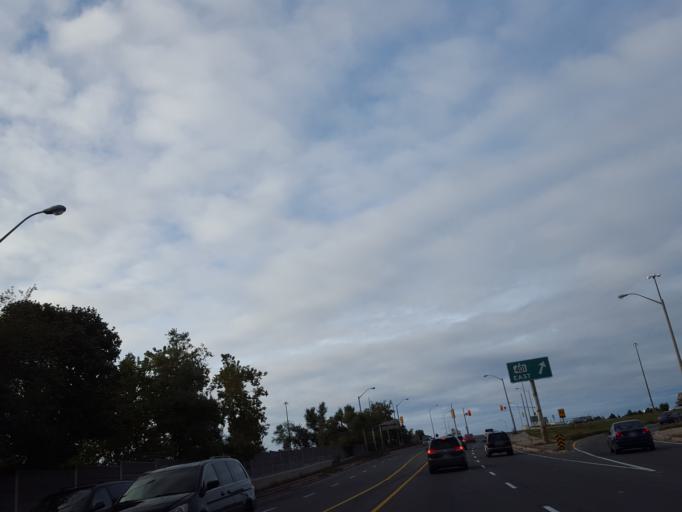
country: CA
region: Ontario
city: Scarborough
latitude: 43.7677
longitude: -79.3030
